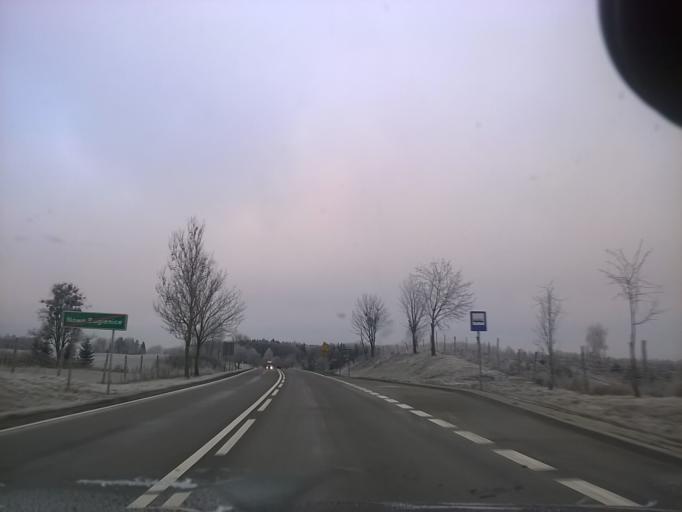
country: PL
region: Warmian-Masurian Voivodeship
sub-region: Powiat mragowski
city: Mragowo
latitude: 53.8388
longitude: 21.2053
